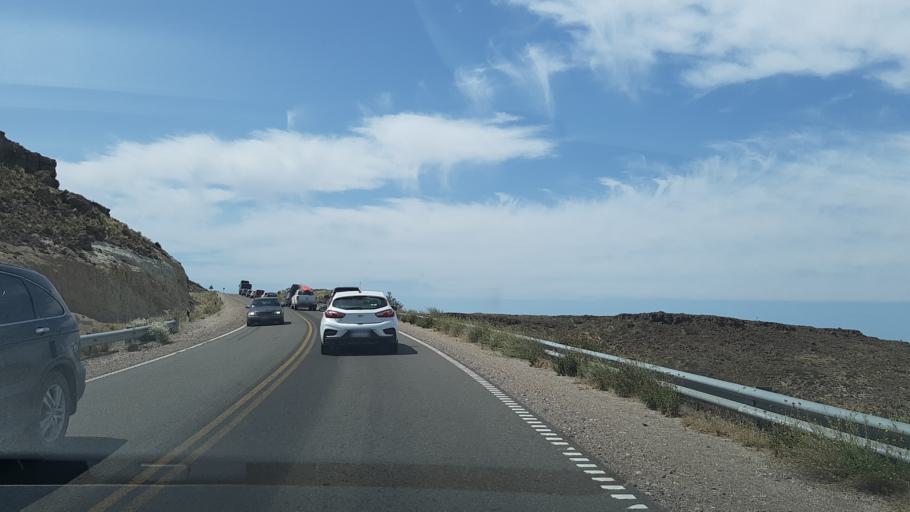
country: AR
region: Neuquen
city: Piedra del Aguila
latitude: -39.9834
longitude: -70.0431
